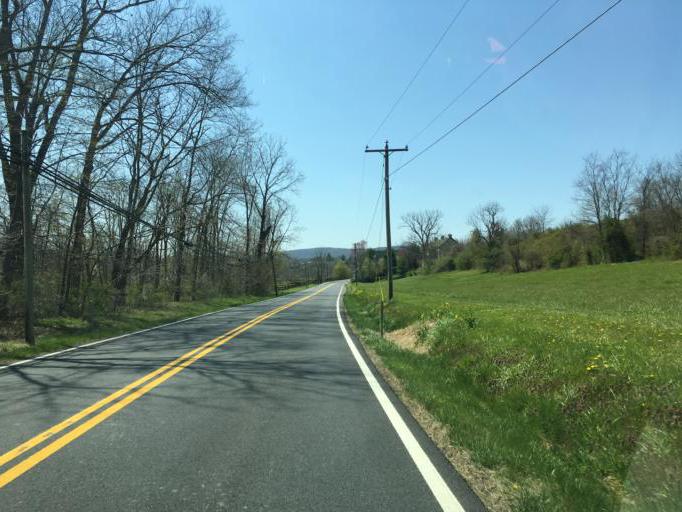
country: US
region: Maryland
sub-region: Frederick County
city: Myersville
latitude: 39.5109
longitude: -77.5543
